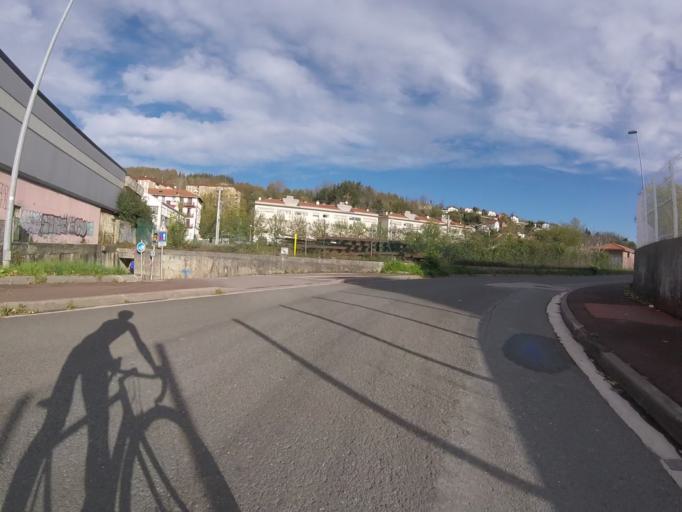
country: ES
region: Basque Country
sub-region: Provincia de Guipuzcoa
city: Hernani
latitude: 43.2716
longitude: -1.9646
